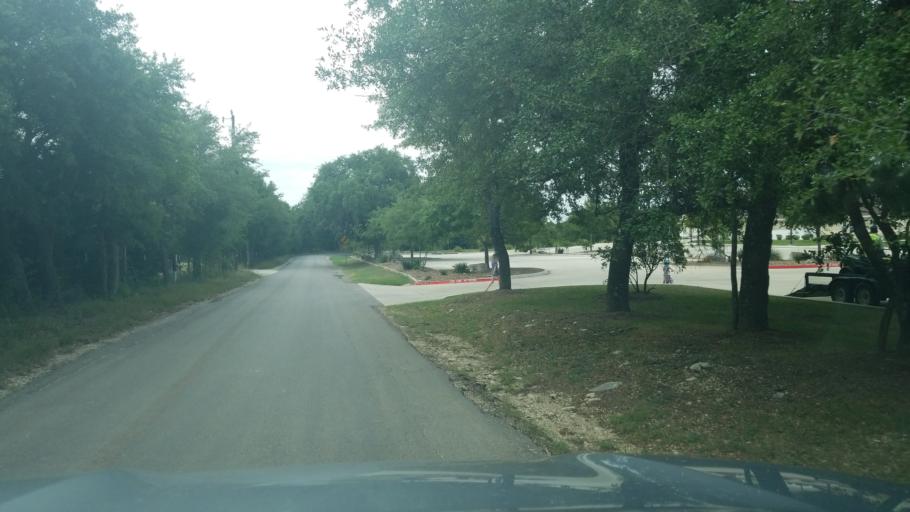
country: US
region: Texas
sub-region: Comal County
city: Bulverde
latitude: 29.7611
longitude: -98.4089
